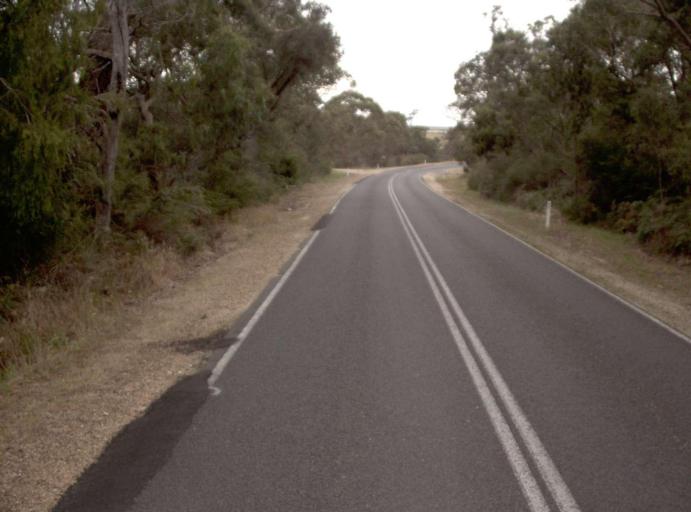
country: AU
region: Victoria
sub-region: Wellington
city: Sale
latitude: -38.1739
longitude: 147.1683
